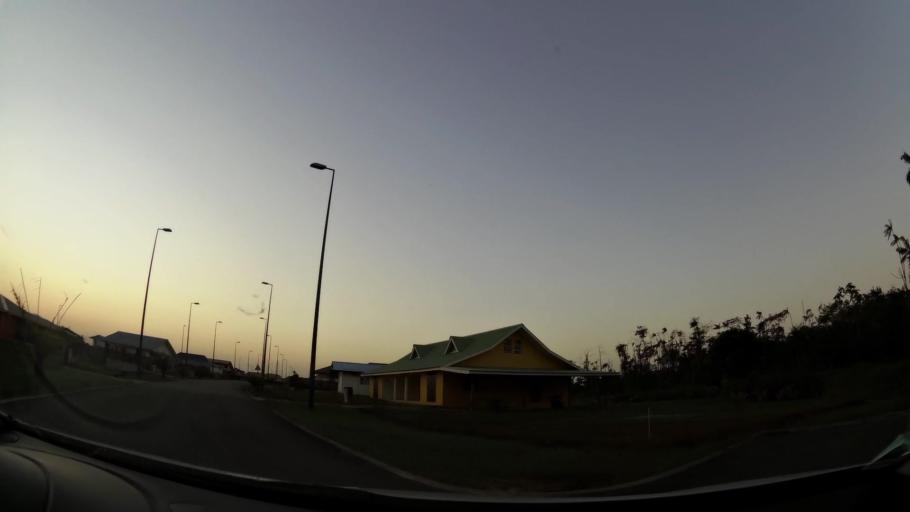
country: GF
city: Macouria
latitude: 4.9229
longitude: -52.4069
